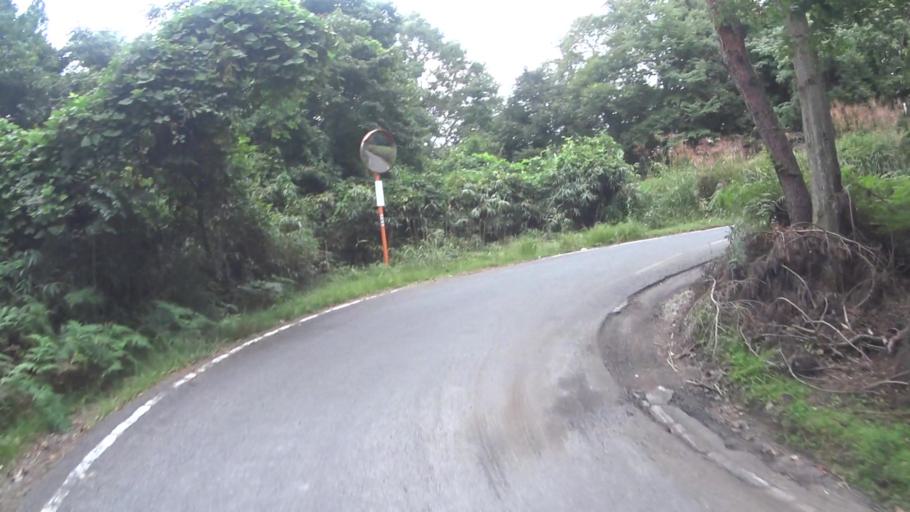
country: JP
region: Kyoto
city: Uji
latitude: 34.8529
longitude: 135.9402
